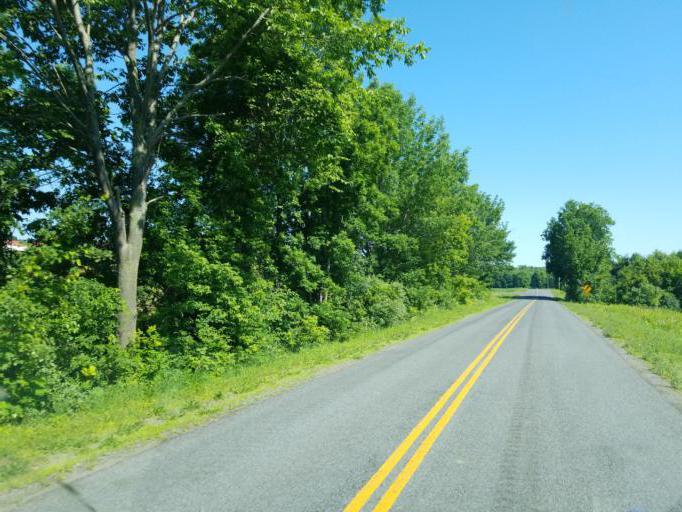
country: US
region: New York
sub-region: Wayne County
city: Clyde
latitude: 43.1349
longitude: -76.8426
